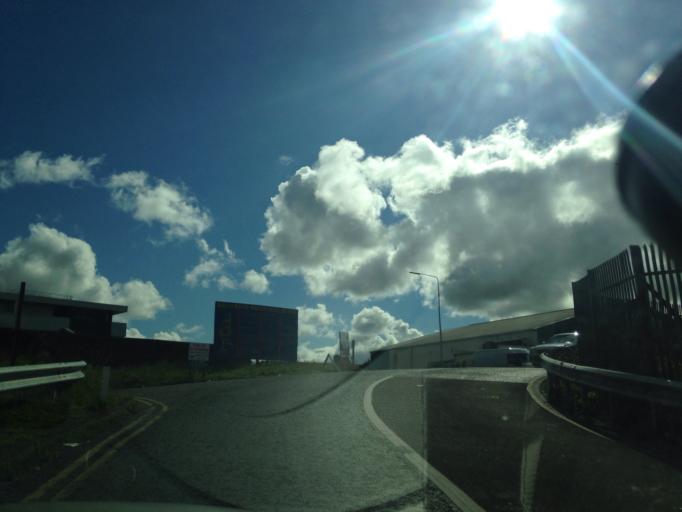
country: IE
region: Connaught
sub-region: County Galway
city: Gaillimh
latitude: 53.2927
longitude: -9.0178
